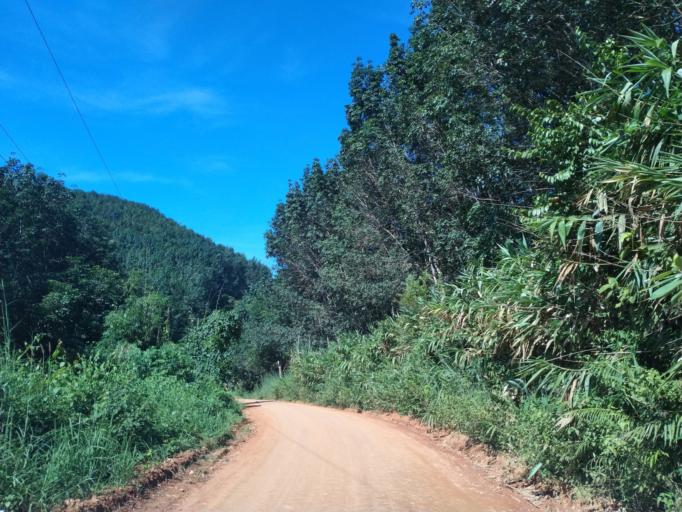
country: TH
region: Changwat Bueng Kan
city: Pak Khat
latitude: 18.6337
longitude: 103.0646
